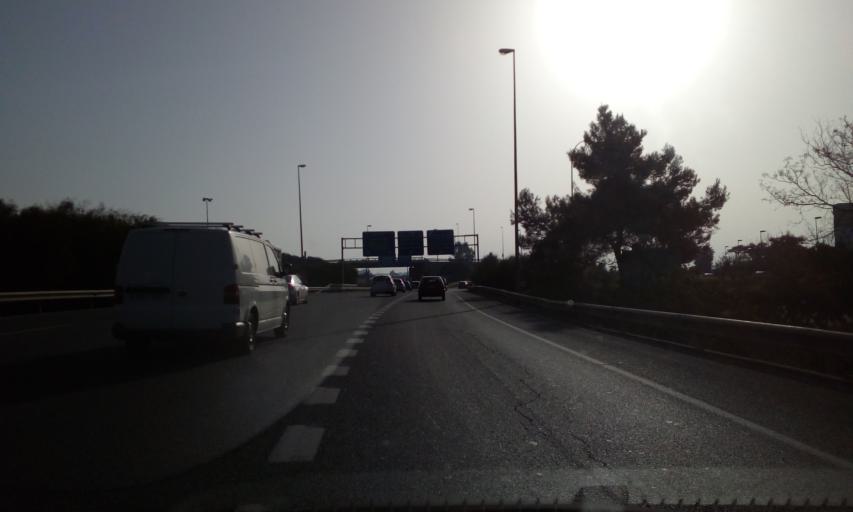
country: ES
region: Andalusia
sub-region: Provincia de Sevilla
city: Camas
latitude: 37.3895
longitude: -6.0299
